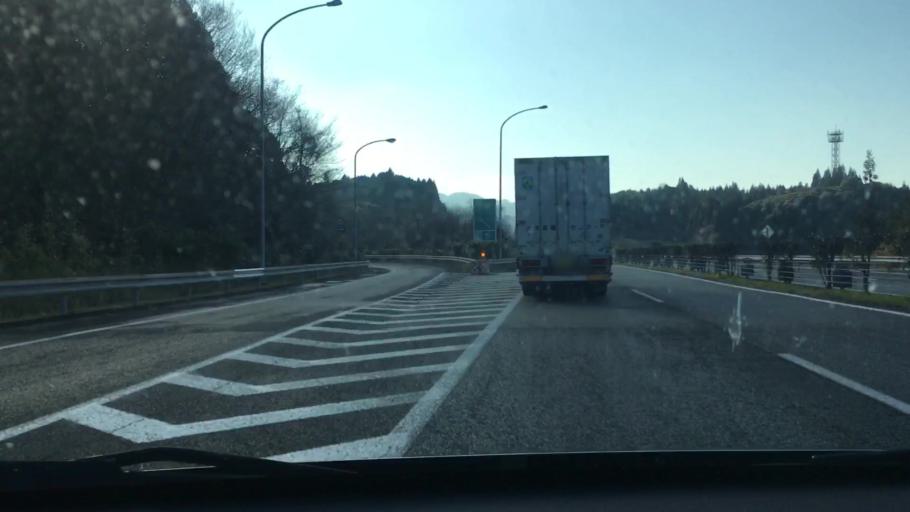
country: JP
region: Kagoshima
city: Okuchi-shinohara
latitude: 31.9453
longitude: 130.7234
